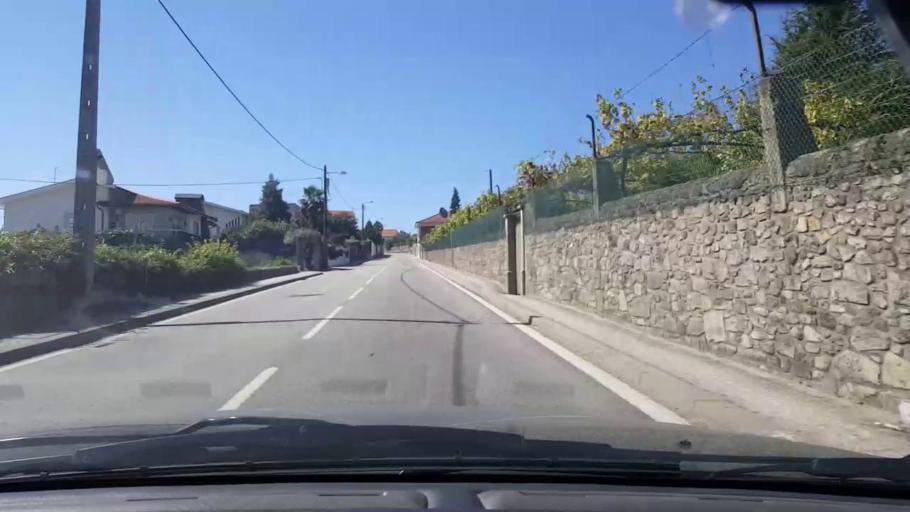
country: PT
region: Porto
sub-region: Vila do Conde
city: Arvore
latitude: 41.3401
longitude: -8.6745
